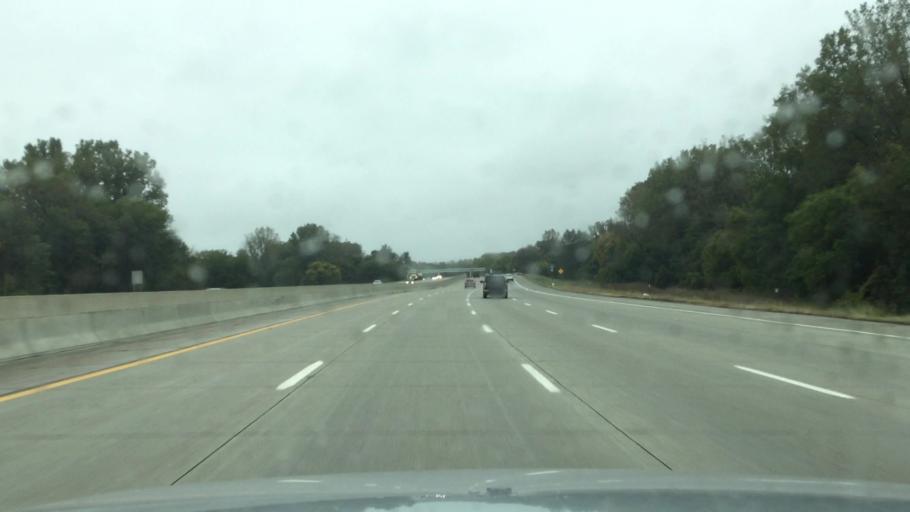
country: US
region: Michigan
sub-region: Saginaw County
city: Bridgeport
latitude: 43.3458
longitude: -83.8636
